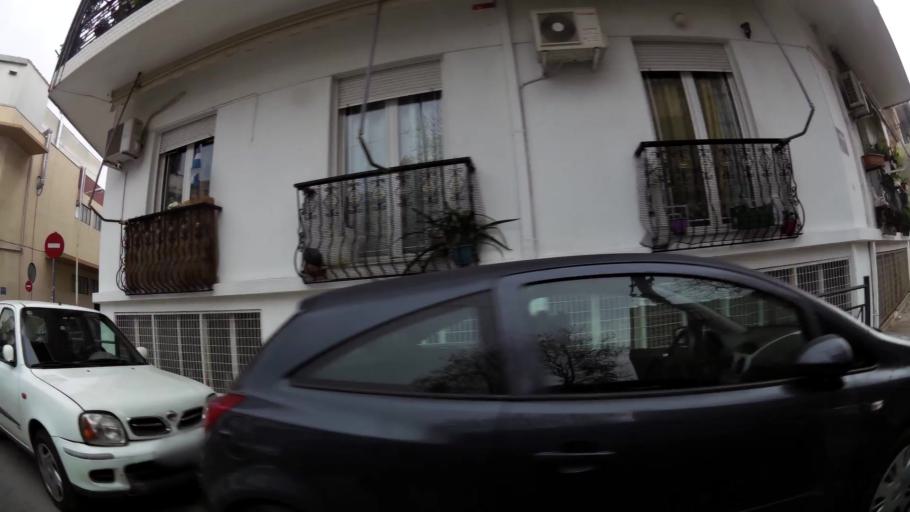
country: GR
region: Attica
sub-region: Nomos Piraios
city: Agios Ioannis Rentis
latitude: 37.9625
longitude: 23.6597
